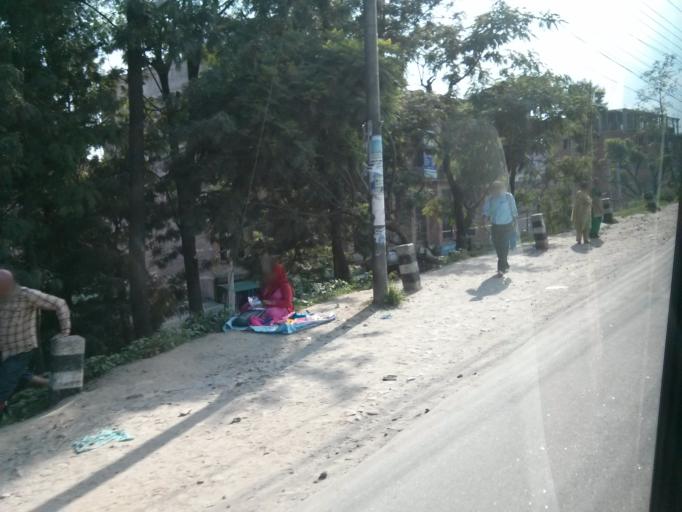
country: NP
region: Central Region
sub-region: Bagmati Zone
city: Kathmandu
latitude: 27.7058
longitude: 85.3462
